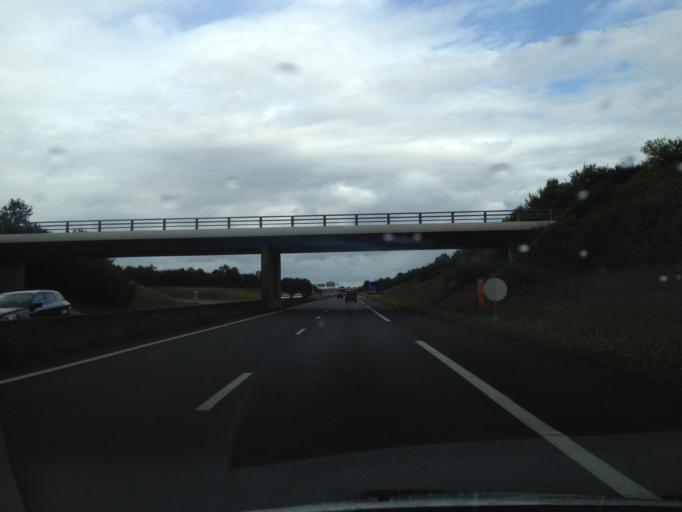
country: FR
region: Pays de la Loire
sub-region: Departement de la Vendee
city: Les Essarts
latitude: 46.7917
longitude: -1.1986
